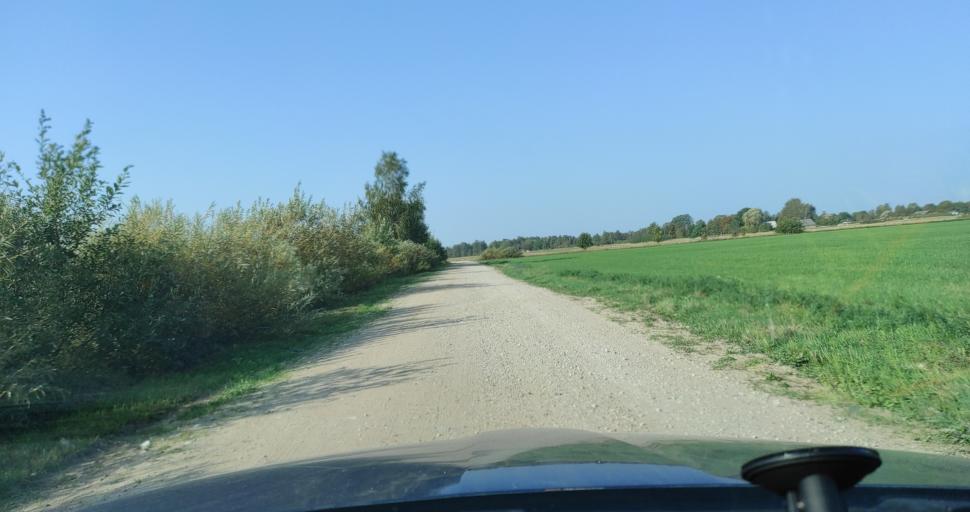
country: LV
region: Ventspils Rajons
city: Piltene
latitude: 57.2239
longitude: 21.6250
